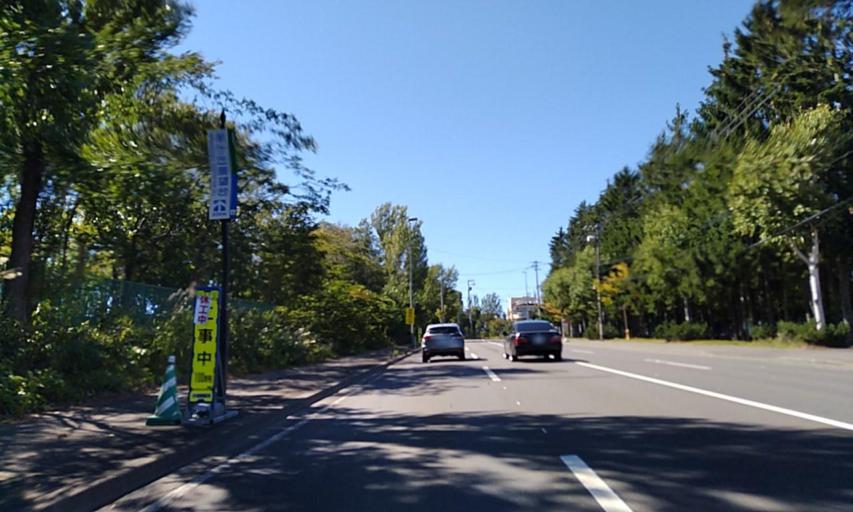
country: JP
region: Hokkaido
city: Sapporo
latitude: 43.0044
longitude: 141.3952
